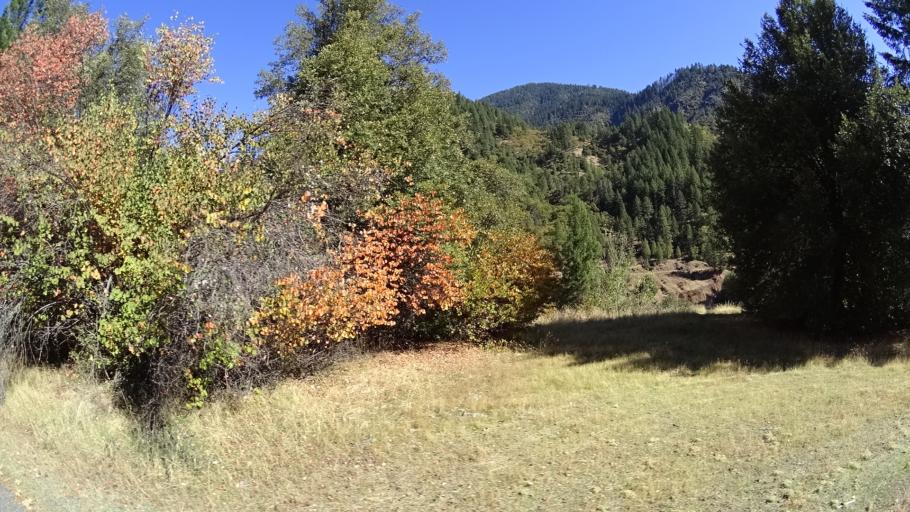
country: US
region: California
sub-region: Humboldt County
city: Willow Creek
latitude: 41.3086
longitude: -123.3749
